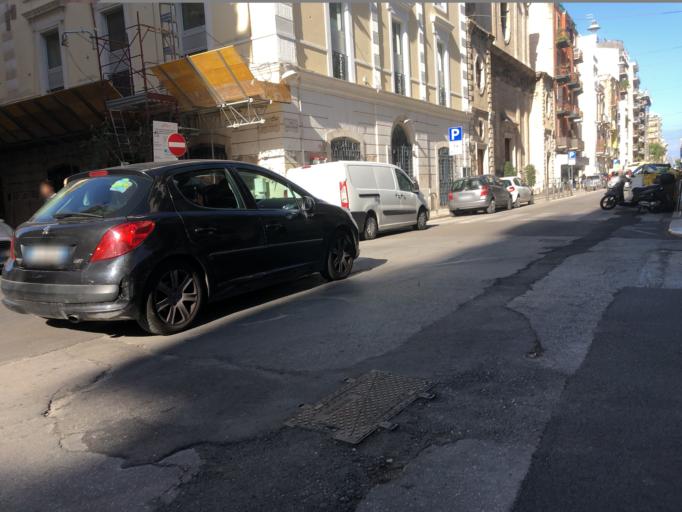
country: IT
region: Apulia
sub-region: Provincia di Bari
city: Bari
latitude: 41.1226
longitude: 16.8633
